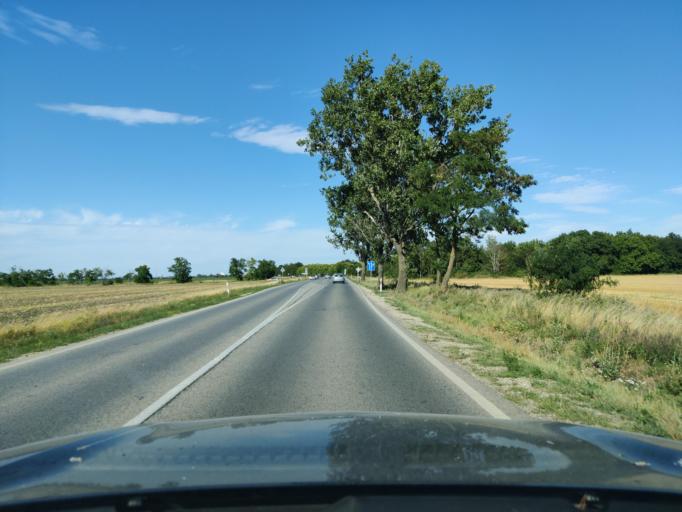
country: HU
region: Gyor-Moson-Sopron
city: Janossomorja
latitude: 47.8243
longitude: 17.2019
